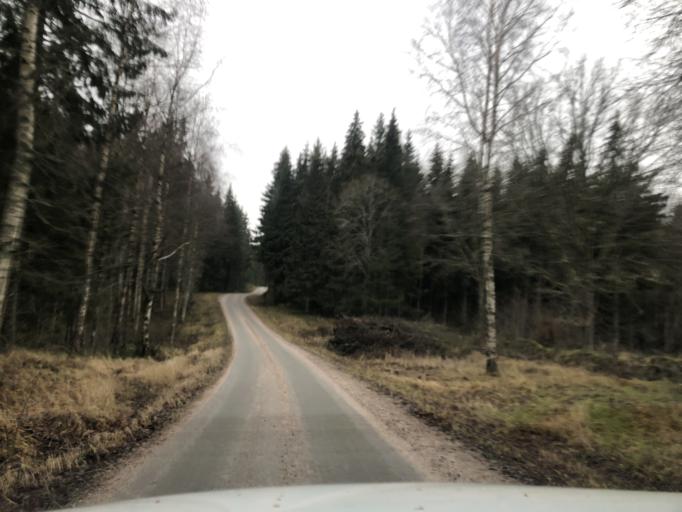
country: SE
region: Vaestra Goetaland
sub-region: Ulricehamns Kommun
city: Ulricehamn
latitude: 57.8759
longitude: 13.5633
